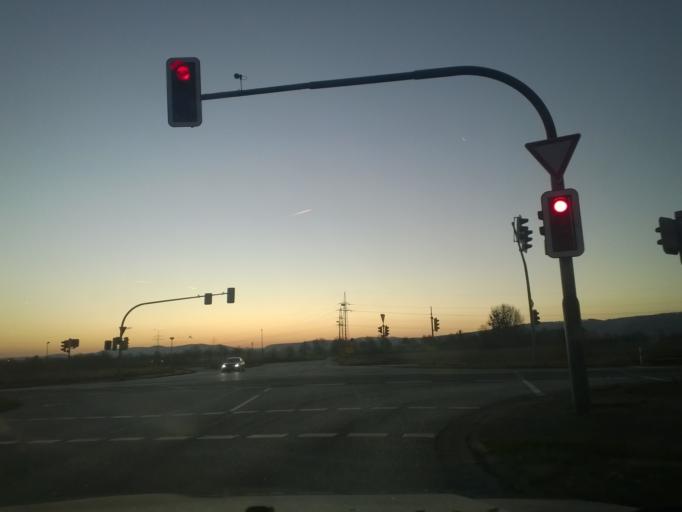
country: DE
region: Lower Saxony
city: Hildesheim
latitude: 52.1204
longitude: 9.9542
